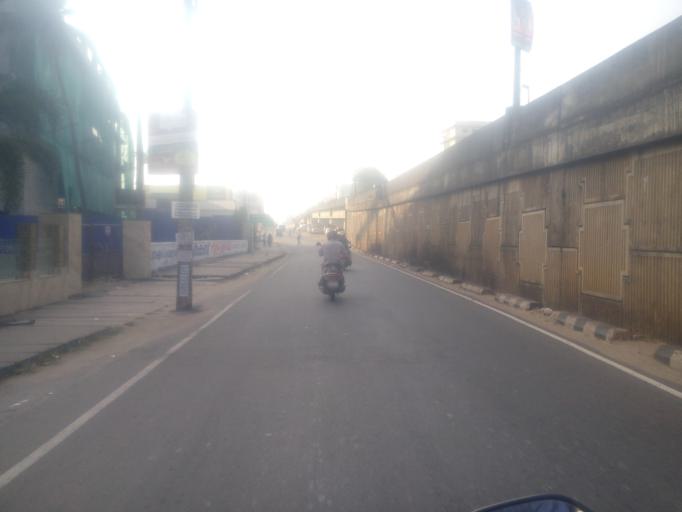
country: IN
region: Kerala
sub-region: Kozhikode
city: Kozhikode
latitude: 11.2587
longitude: 75.7938
